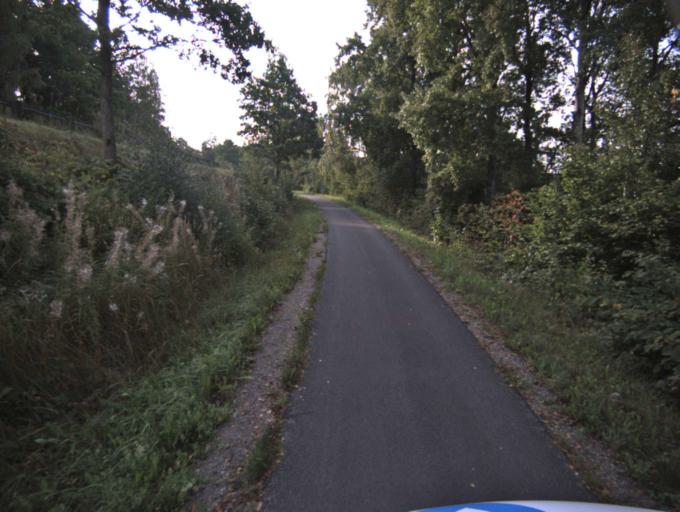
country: SE
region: Vaestra Goetaland
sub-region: Ulricehamns Kommun
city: Ulricehamn
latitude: 57.7437
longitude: 13.3942
